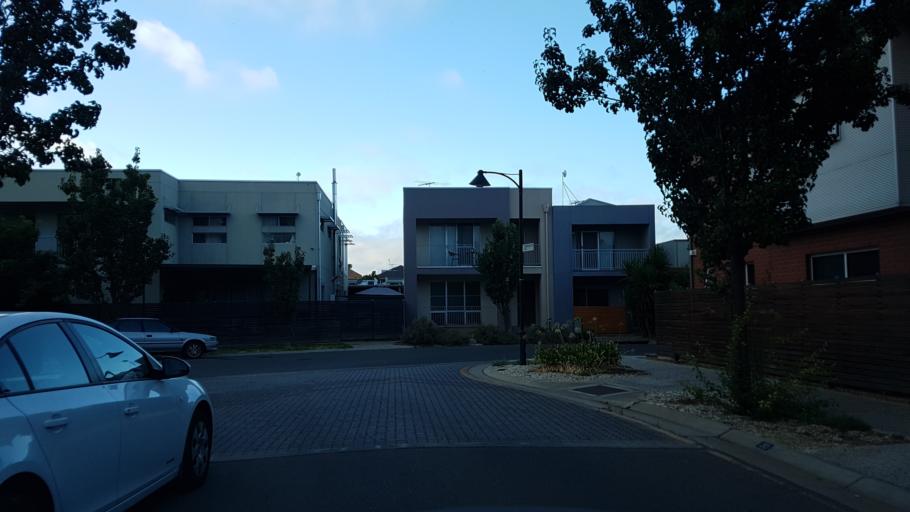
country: AU
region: South Australia
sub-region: Salisbury
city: Ingle Farm
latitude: -34.8067
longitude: 138.6112
